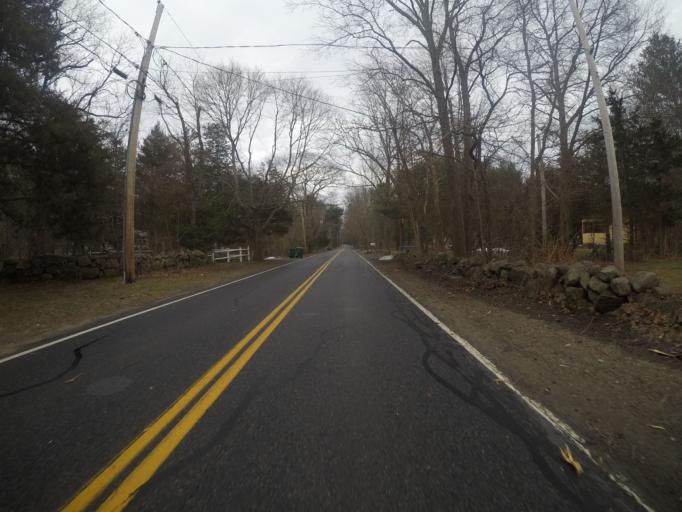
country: US
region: Massachusetts
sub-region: Bristol County
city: Easton
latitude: 42.0430
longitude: -71.1482
